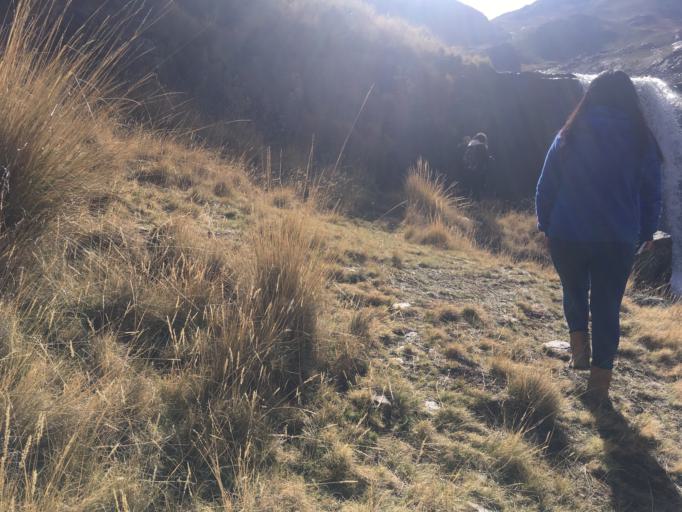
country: BO
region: La Paz
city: La Paz
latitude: -16.4026
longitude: -68.0157
